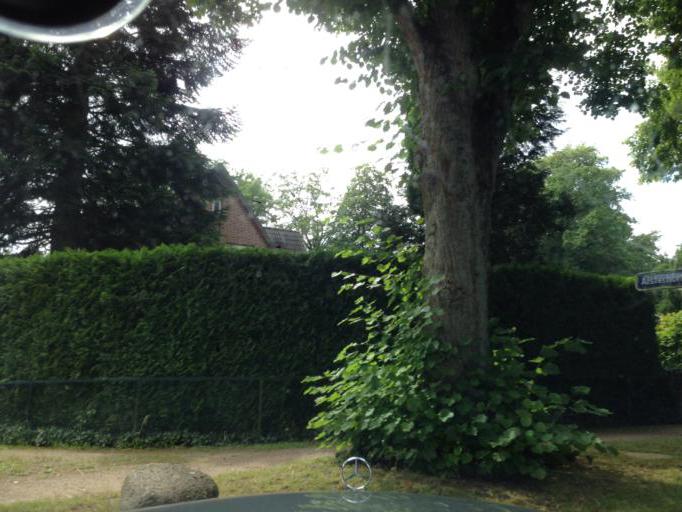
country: DE
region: Hamburg
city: Wohldorf-Ohlstedt
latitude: 53.7006
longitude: 10.1217
